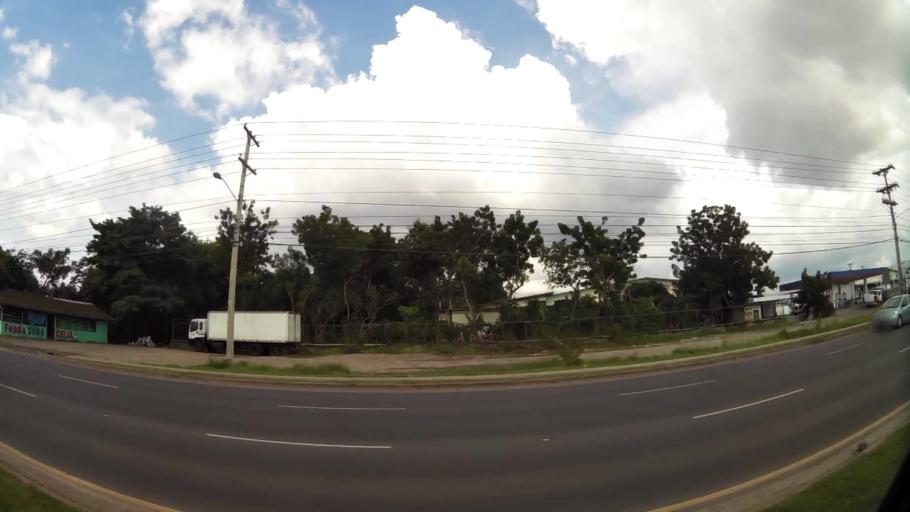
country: PA
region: Panama
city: Tocumen
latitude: 9.0679
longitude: -79.4099
